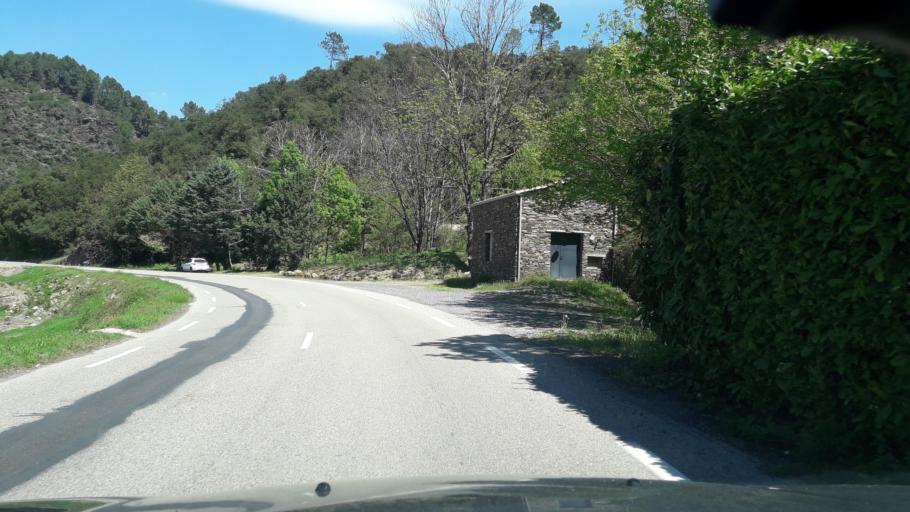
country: FR
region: Languedoc-Roussillon
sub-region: Departement du Gard
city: Lasalle
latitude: 44.1132
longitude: 3.7726
